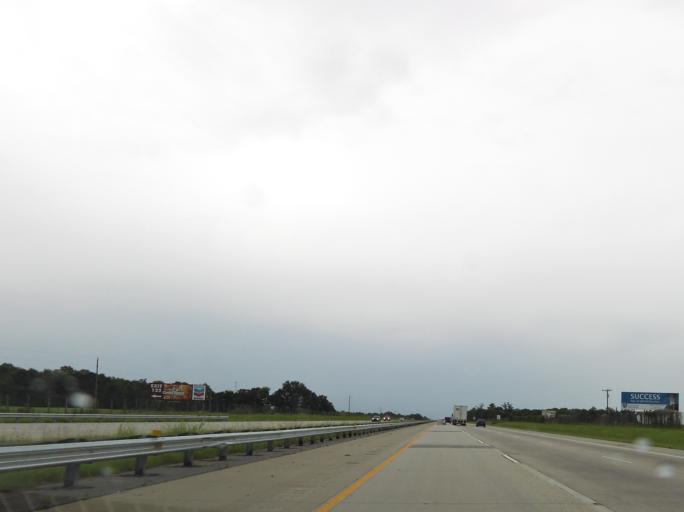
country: US
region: Georgia
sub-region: Dooly County
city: Unadilla
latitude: 32.2866
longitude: -83.7578
